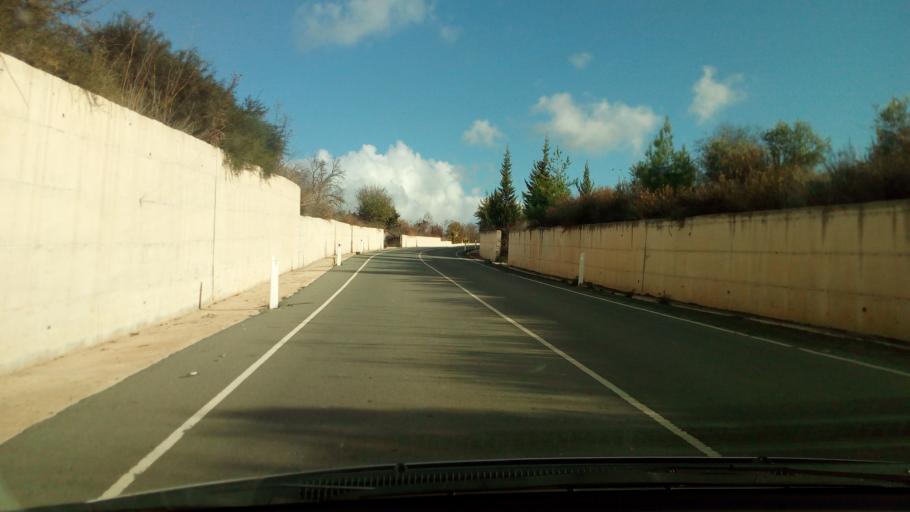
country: CY
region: Pafos
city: Tala
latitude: 34.9320
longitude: 32.5185
